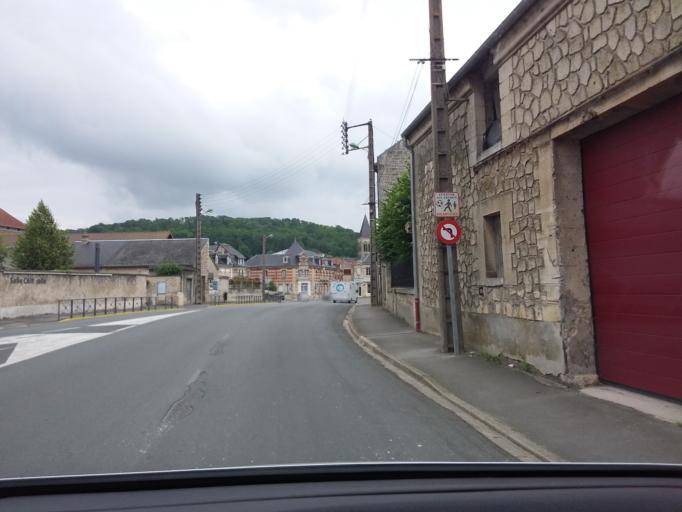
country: FR
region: Picardie
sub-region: Departement de l'Aisne
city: Vailly-sur-Aisne
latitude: 49.4075
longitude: 3.5158
